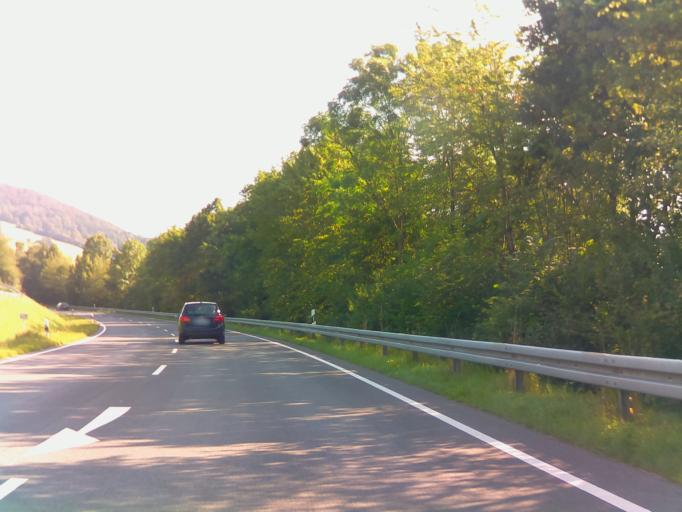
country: DE
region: Bavaria
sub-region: Regierungsbezirk Unterfranken
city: Wildflecken
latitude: 50.3532
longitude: 9.8850
